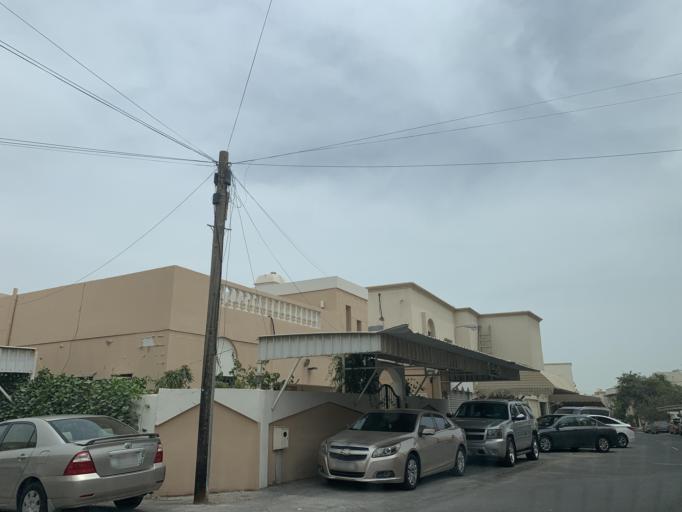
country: BH
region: Northern
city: Ar Rifa'
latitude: 26.1393
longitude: 50.5562
